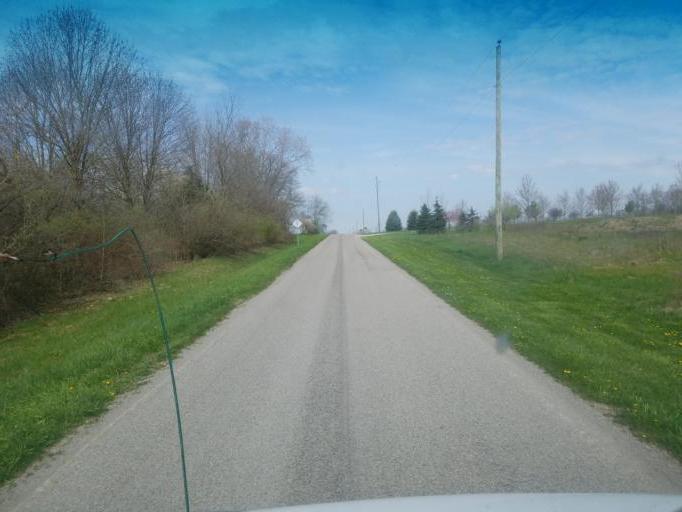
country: US
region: Ohio
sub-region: Union County
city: Richwood
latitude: 40.4815
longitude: -83.4397
